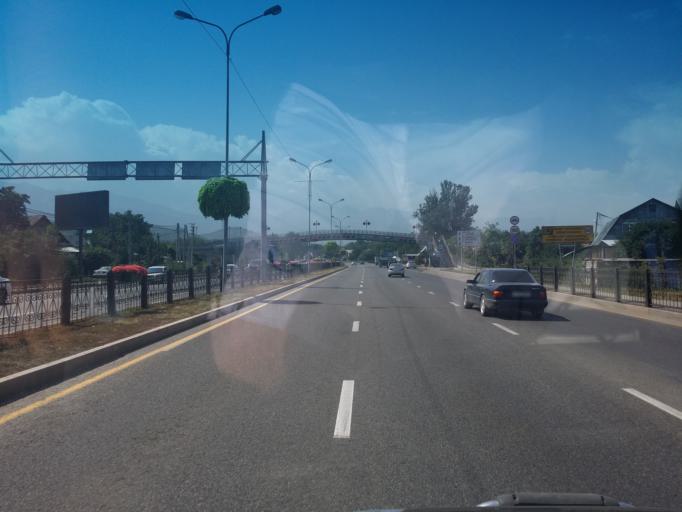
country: KZ
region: Almaty Qalasy
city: Almaty
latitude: 43.2809
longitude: 76.9857
